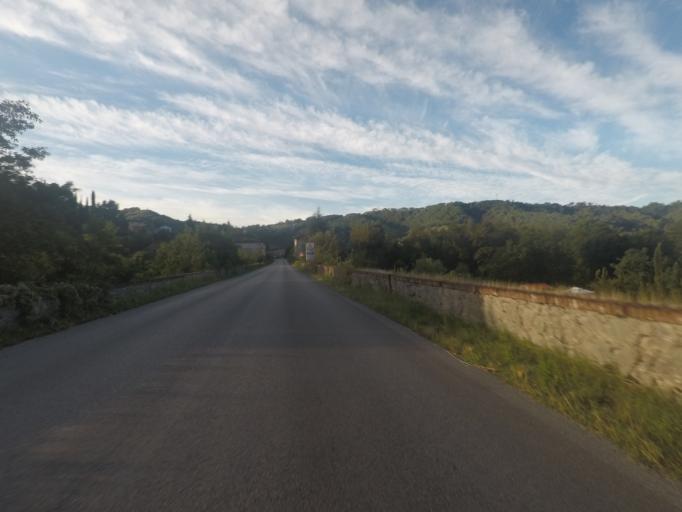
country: IT
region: Tuscany
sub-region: Provincia di Lucca
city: Stiava
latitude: 43.9202
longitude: 10.3338
